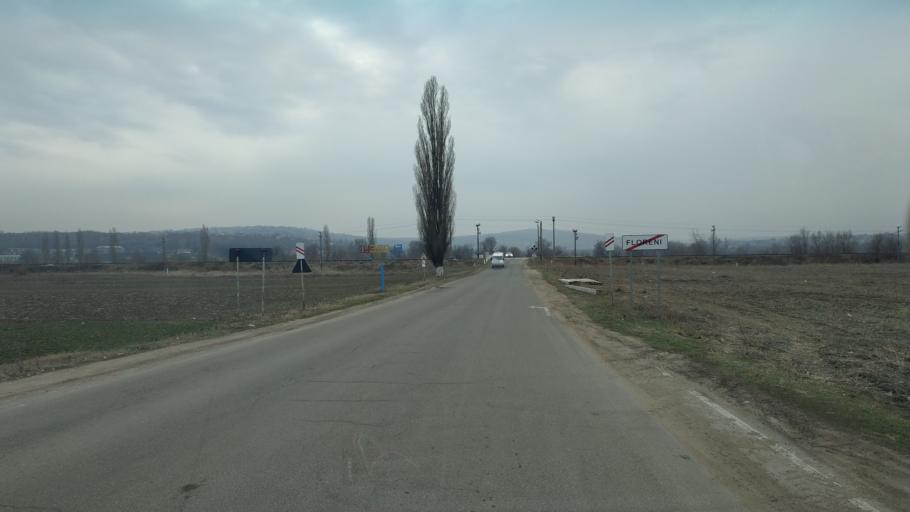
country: MD
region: Chisinau
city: Singera
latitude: 46.9323
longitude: 28.9855
